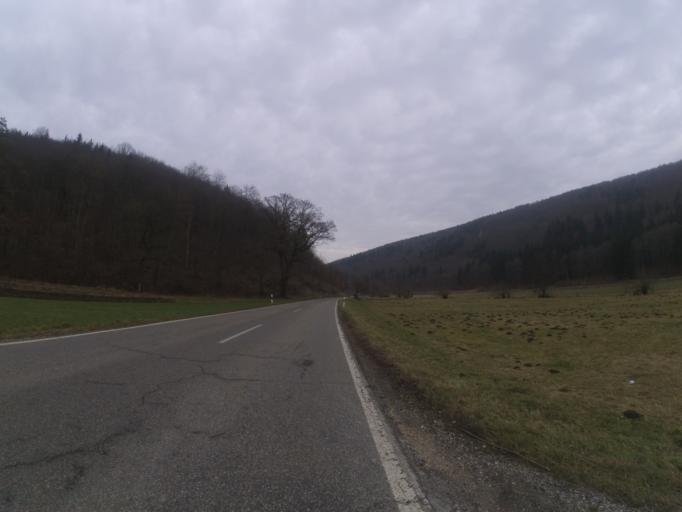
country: DE
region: Baden-Wuerttemberg
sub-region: Tuebingen Region
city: Schelklingen
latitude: 48.3692
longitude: 9.6861
